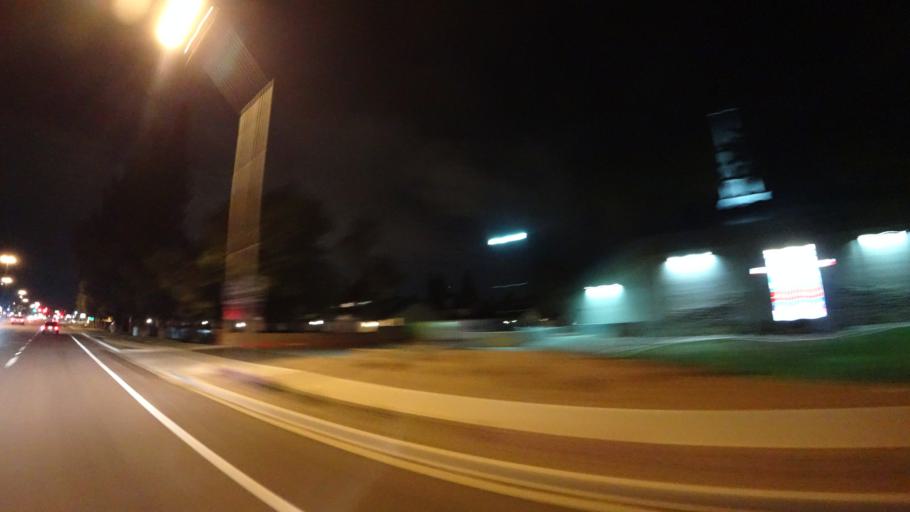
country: US
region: Arizona
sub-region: Maricopa County
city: Gilbert
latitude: 33.3646
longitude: -111.7859
